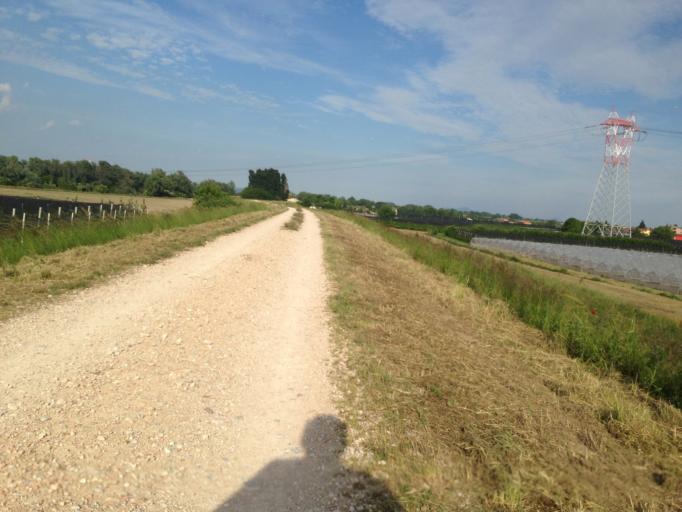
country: IT
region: Veneto
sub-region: Provincia di Verona
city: Belfiore
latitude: 45.3684
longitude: 11.1781
